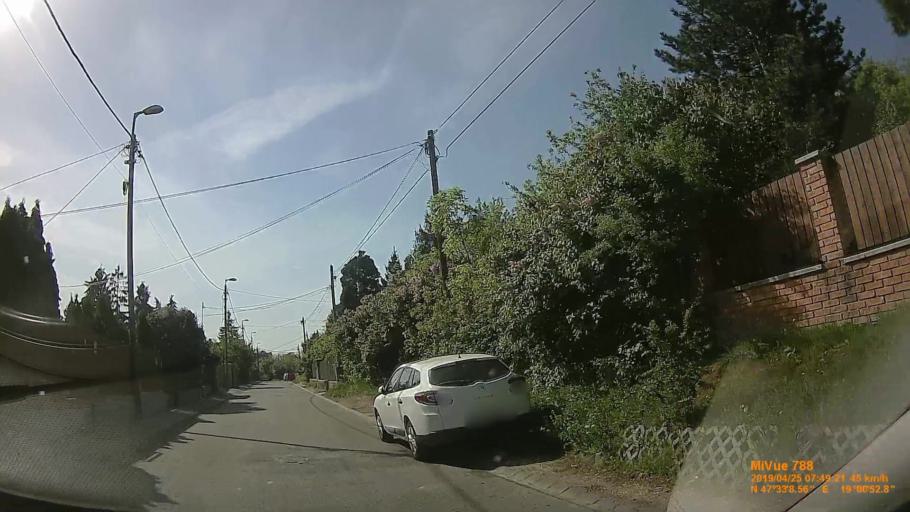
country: HU
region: Budapest
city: Budapest III. keruelet
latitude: 47.5523
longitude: 19.0147
